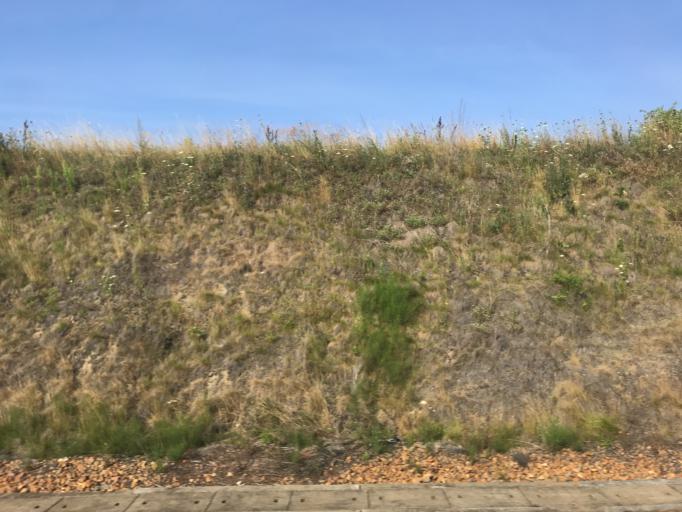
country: CZ
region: Jihocesky
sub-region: Okres Tabor
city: Tabor
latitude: 49.4203
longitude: 14.6704
